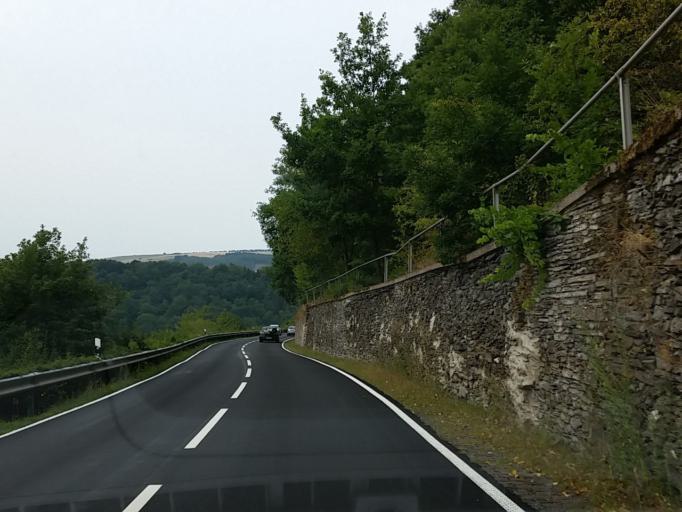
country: DE
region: Rheinland-Pfalz
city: Morscheid
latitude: 49.7348
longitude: 6.7660
